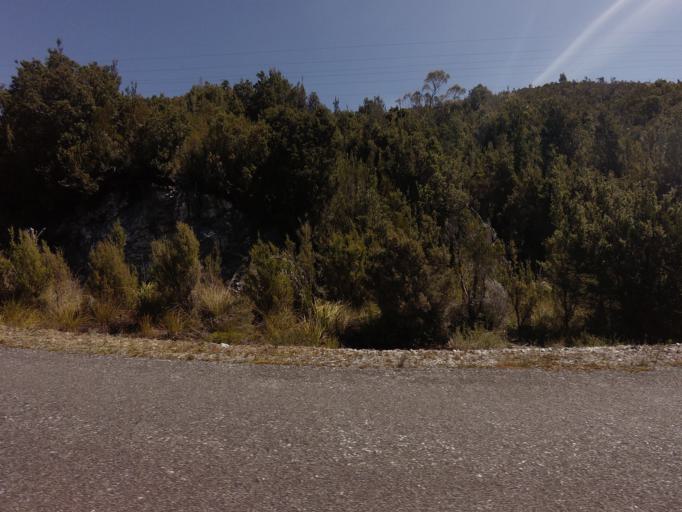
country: AU
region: Tasmania
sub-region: West Coast
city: Queenstown
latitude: -42.7460
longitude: 145.9808
